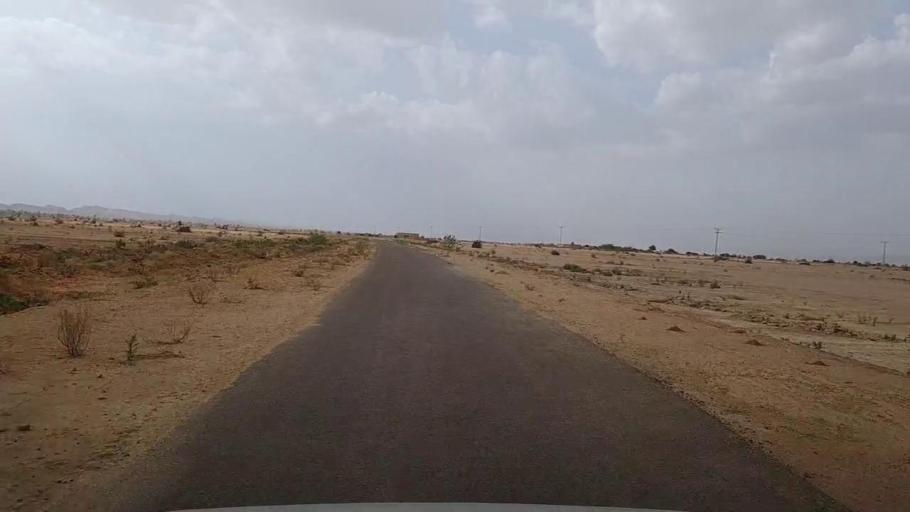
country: PK
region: Sindh
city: Jamshoro
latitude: 25.4676
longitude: 67.6771
